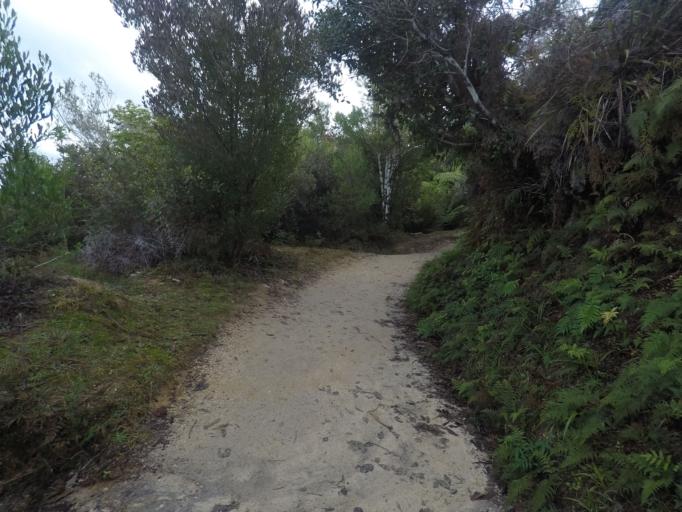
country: NZ
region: Tasman
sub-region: Tasman District
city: Motueka
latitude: -40.9905
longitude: 173.0158
